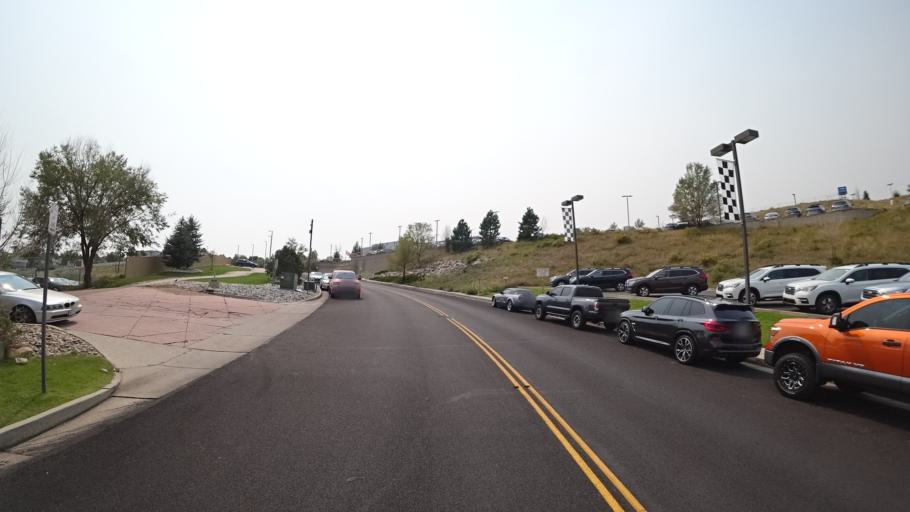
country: US
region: Colorado
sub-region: El Paso County
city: Colorado Springs
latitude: 38.8179
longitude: -104.8368
